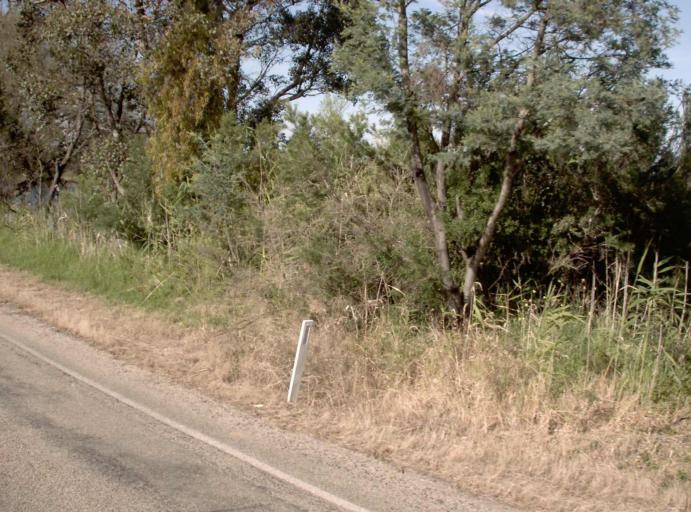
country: AU
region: Victoria
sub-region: East Gippsland
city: Lakes Entrance
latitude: -37.8347
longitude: 147.8621
